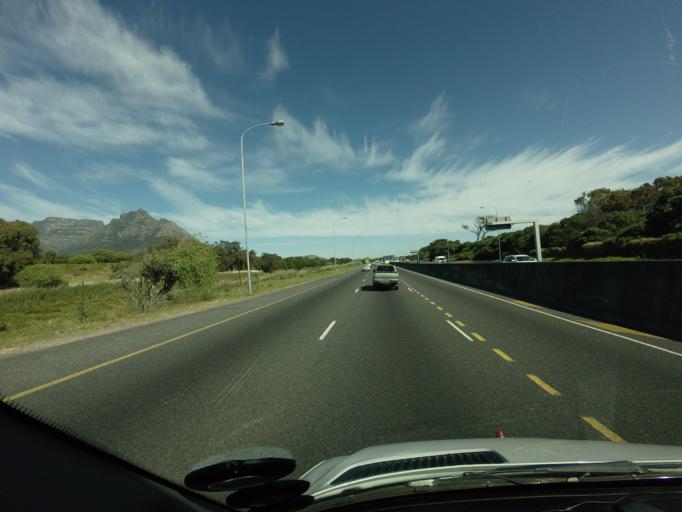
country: ZA
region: Western Cape
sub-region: City of Cape Town
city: Rosebank
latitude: -33.9492
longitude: 18.4905
